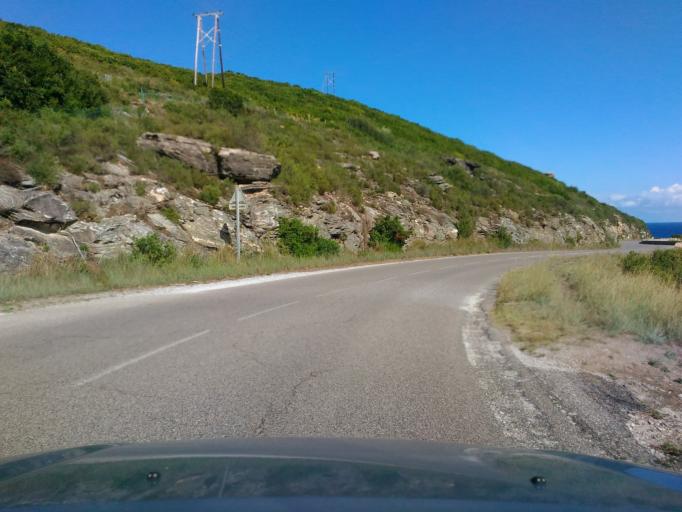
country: FR
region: Corsica
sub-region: Departement de la Haute-Corse
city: Brando
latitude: 42.8006
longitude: 9.4900
